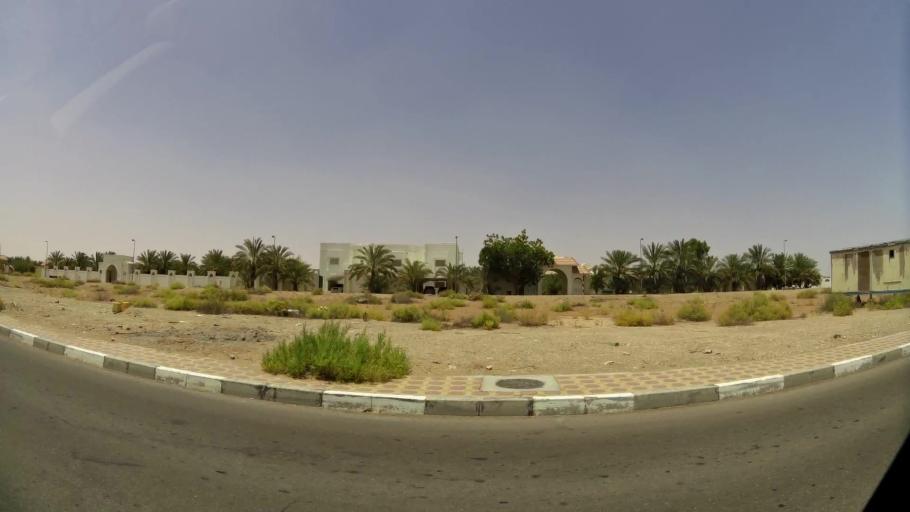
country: OM
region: Al Buraimi
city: Al Buraymi
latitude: 24.2593
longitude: 55.7090
